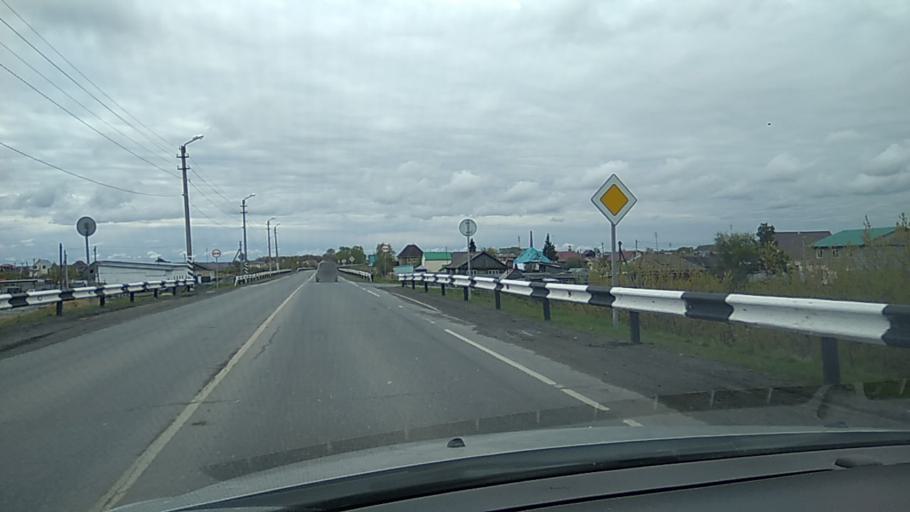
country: RU
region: Tjumen
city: Chervishevo
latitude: 56.9560
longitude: 65.4354
